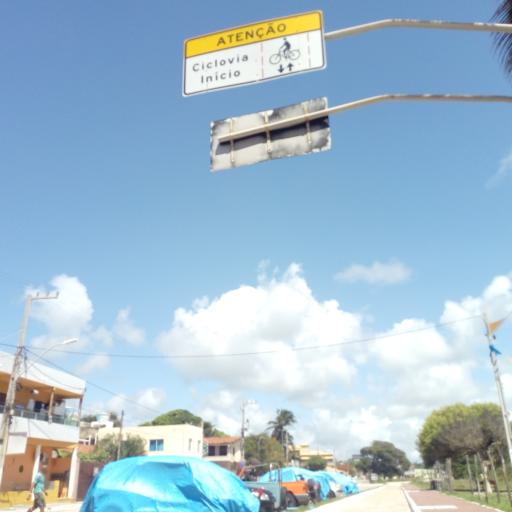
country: BR
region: Pernambuco
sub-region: Sirinhaem
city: Sirinhaem
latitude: -8.5254
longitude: -35.0079
